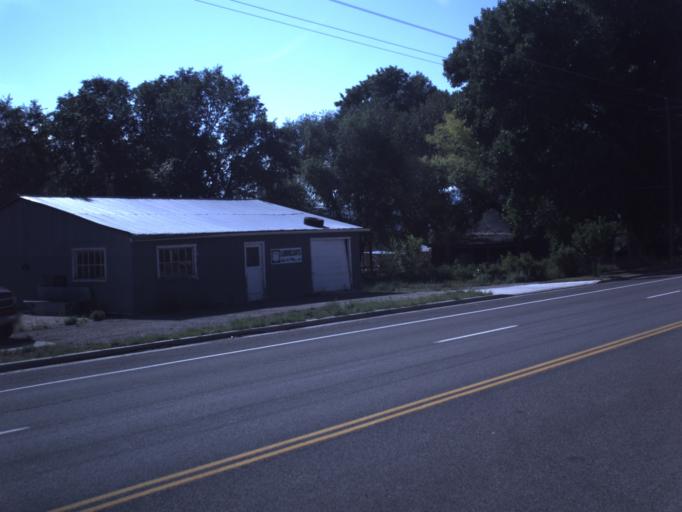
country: US
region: Utah
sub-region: Wayne County
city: Loa
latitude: 38.4066
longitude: -111.6429
